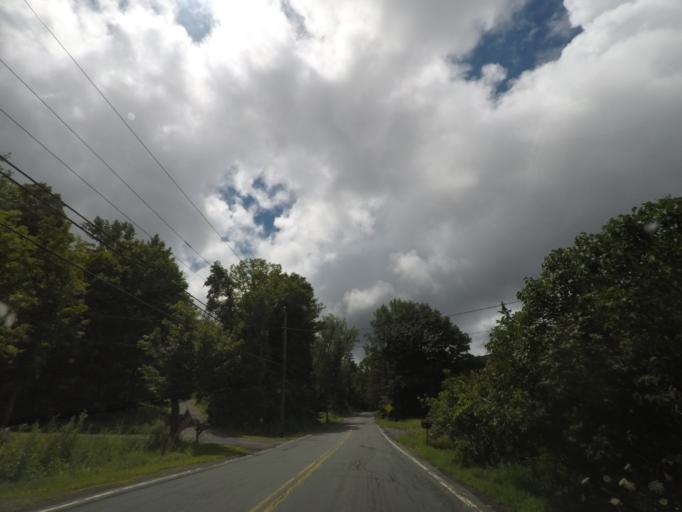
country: US
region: Massachusetts
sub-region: Berkshire County
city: Williamstown
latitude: 42.6918
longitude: -73.3779
